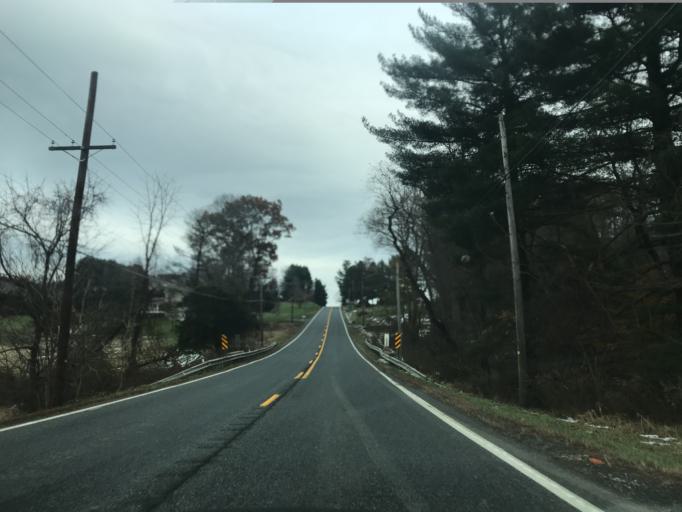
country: US
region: Pennsylvania
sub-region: York County
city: Susquehanna Trails
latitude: 39.6783
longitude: -76.3670
